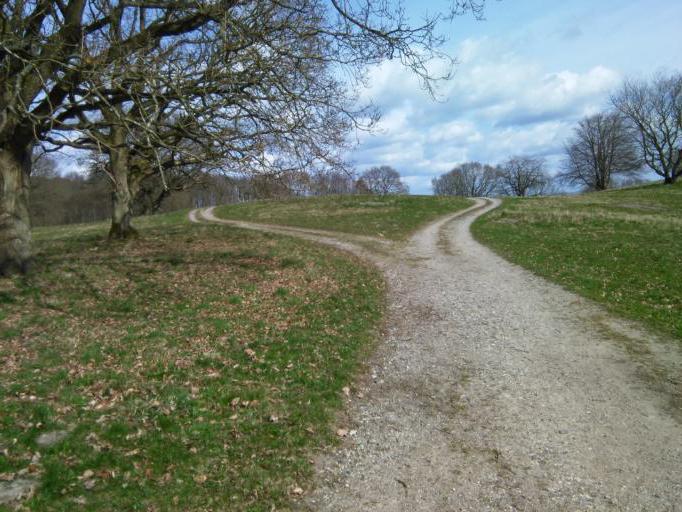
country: DK
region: Central Jutland
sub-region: Arhus Kommune
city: Beder
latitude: 56.0916
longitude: 10.2457
